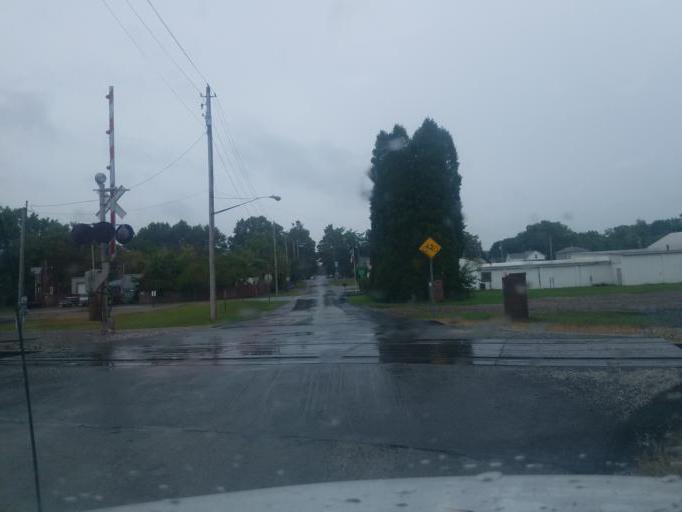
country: US
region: Ohio
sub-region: Wayne County
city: Creston
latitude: 40.9835
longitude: -81.8935
